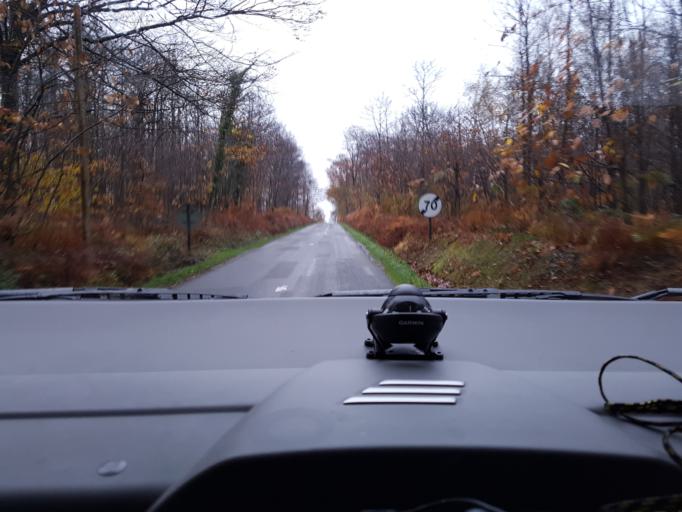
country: FR
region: Brittany
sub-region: Departement d'Ille-et-Vilaine
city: Erbree
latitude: 48.1316
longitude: -1.1551
